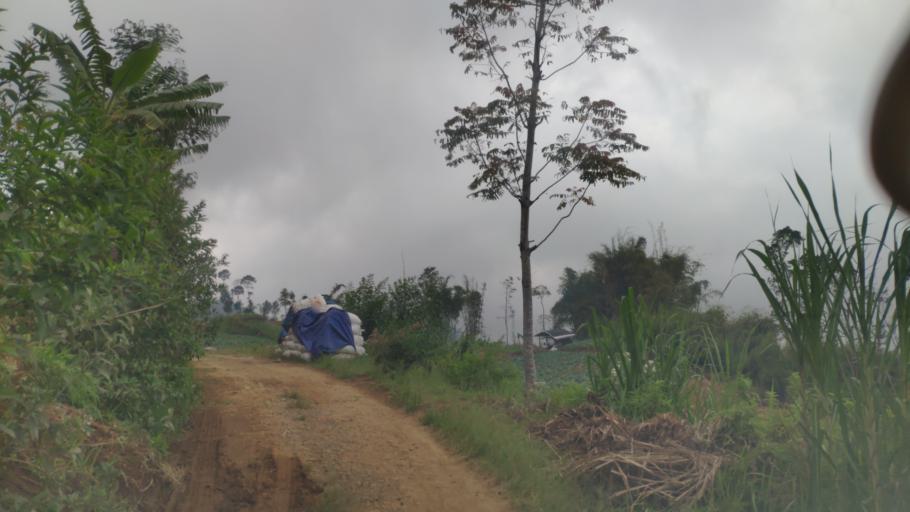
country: ID
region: Central Java
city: Wonosobo
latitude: -7.2326
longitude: 109.8316
